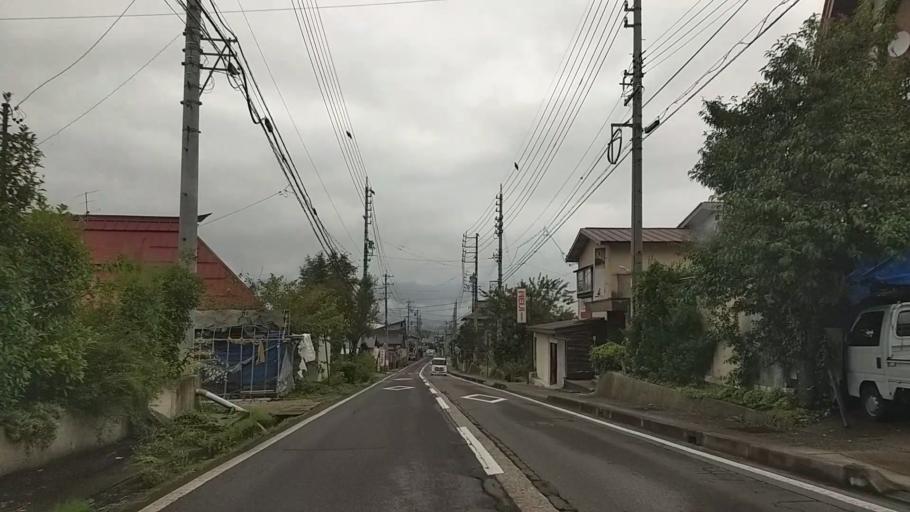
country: JP
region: Nagano
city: Iiyama
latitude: 36.8365
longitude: 138.4092
